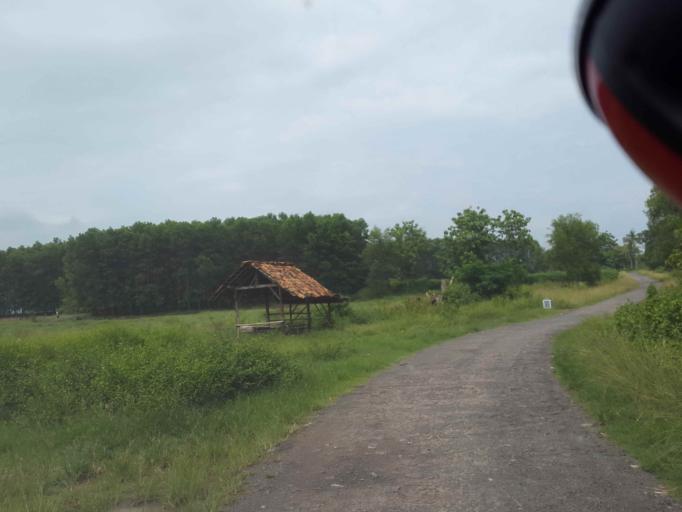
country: ID
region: Lampung
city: Natar
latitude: -5.2542
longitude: 105.2047
